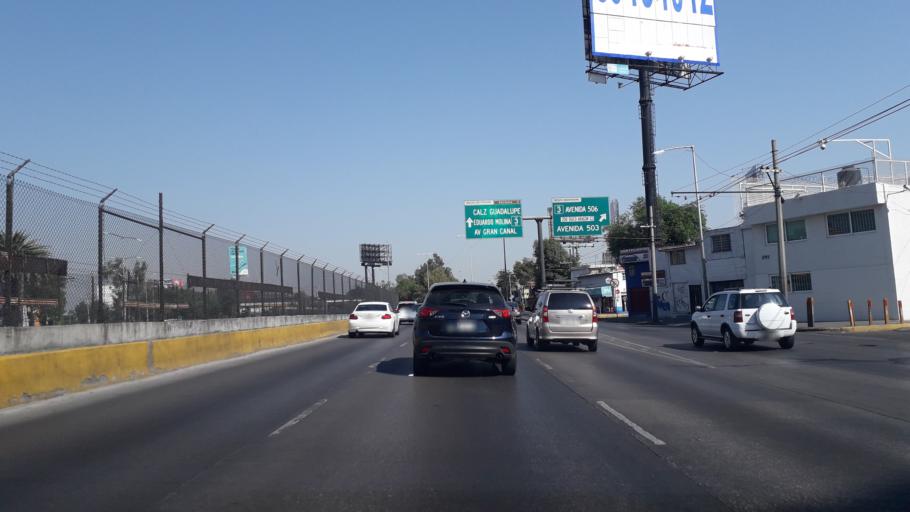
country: MX
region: Mexico City
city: Venustiano Carranza
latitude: 19.4508
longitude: -99.0920
